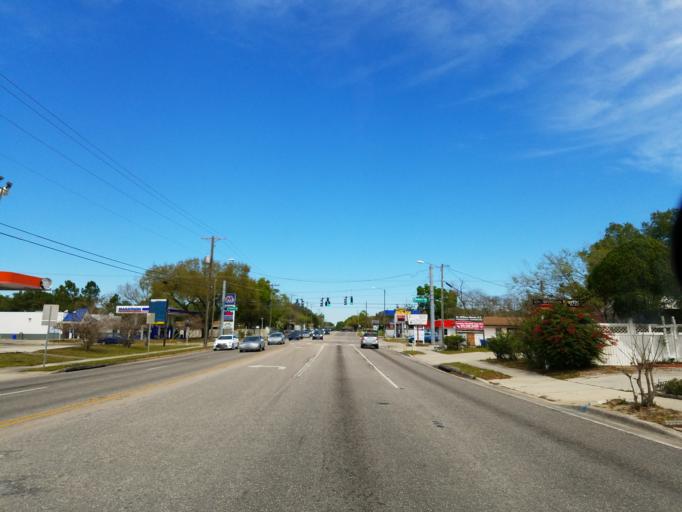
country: US
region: Florida
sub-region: Hillsborough County
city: Brandon
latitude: 27.9589
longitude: -82.2859
